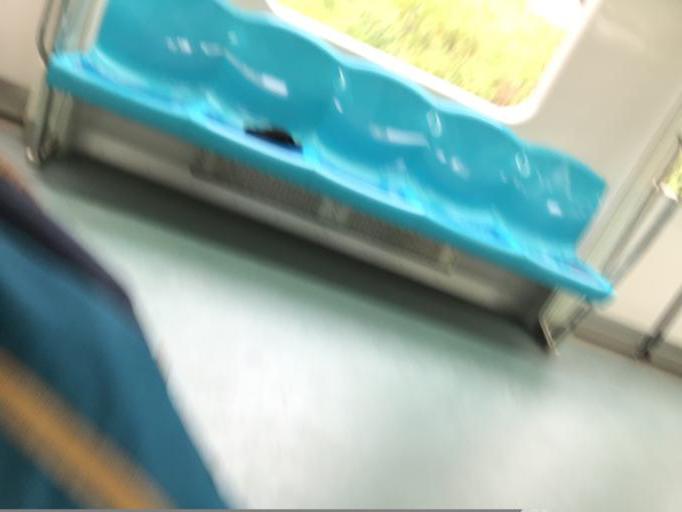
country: TR
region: Kocaeli
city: Darica
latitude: 40.7842
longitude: 29.4098
